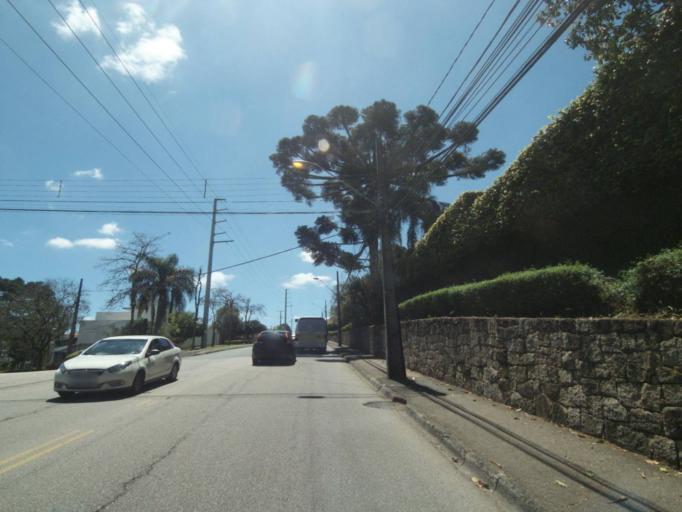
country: BR
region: Parana
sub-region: Curitiba
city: Curitiba
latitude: -25.3925
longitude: -49.2727
